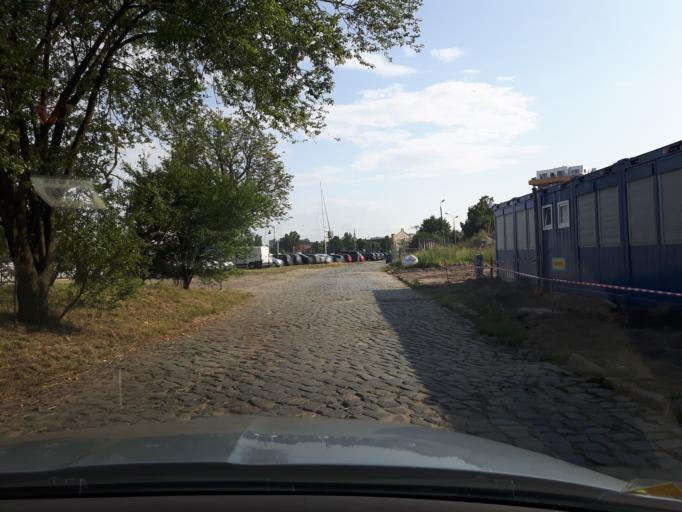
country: PL
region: Pomeranian Voivodeship
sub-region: Gdansk
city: Gdansk
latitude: 54.3566
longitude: 18.6655
